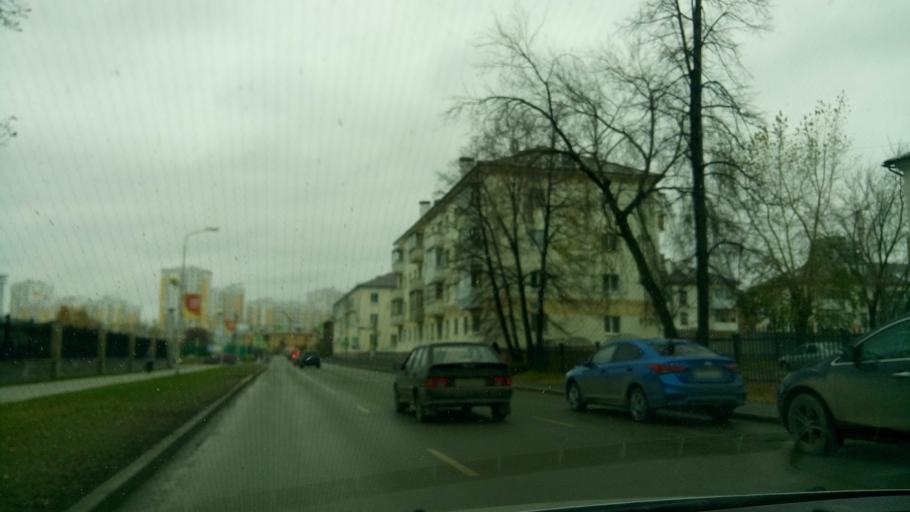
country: RU
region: Sverdlovsk
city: Verkhnyaya Pyshma
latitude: 56.9682
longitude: 60.5799
